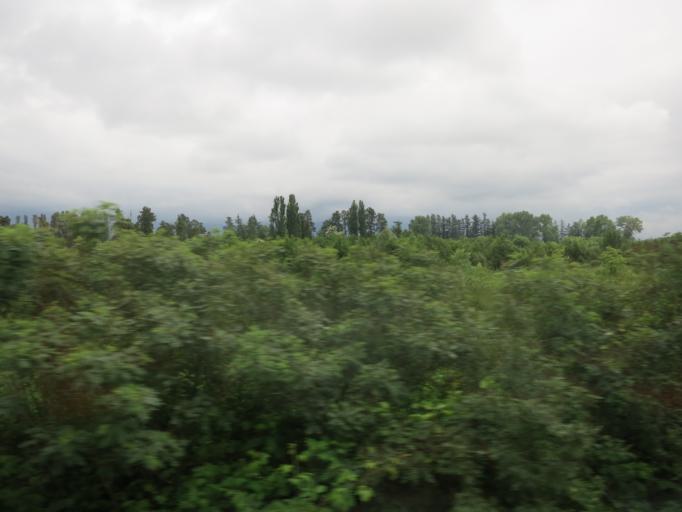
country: GE
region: Ajaria
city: Kobuleti
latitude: 41.8256
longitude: 41.8023
